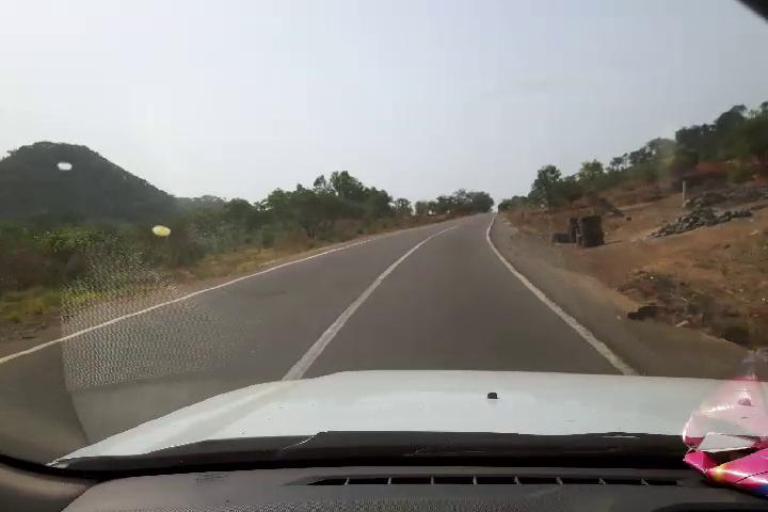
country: SL
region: Western Area
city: Waterloo
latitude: 8.2083
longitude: -13.1326
